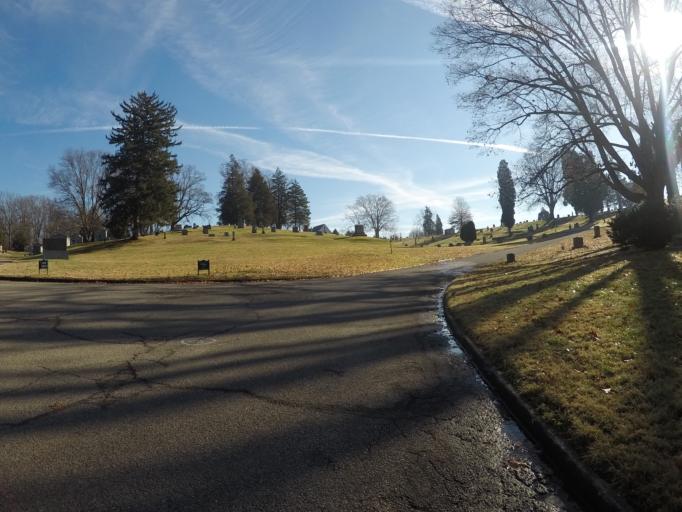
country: US
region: West Virginia
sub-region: Cabell County
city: Huntington
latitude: 38.4103
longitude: -82.4149
